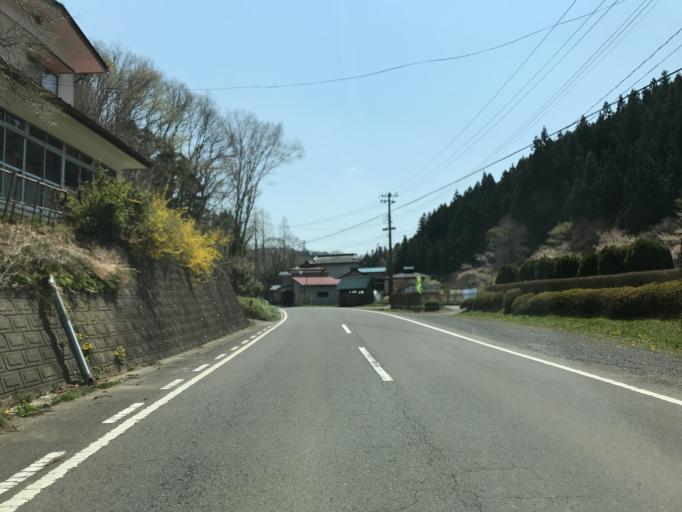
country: JP
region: Fukushima
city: Ishikawa
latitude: 37.0522
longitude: 140.4647
